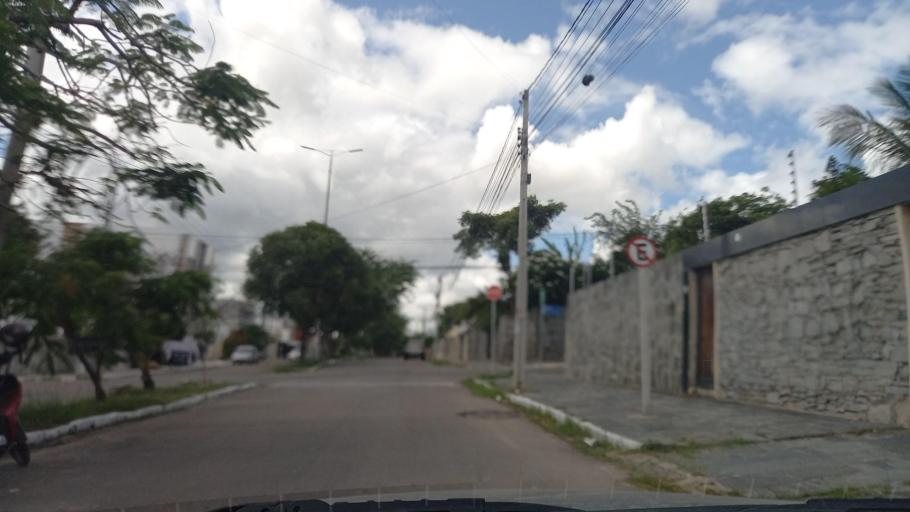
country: BR
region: Pernambuco
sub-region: Caruaru
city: Caruaru
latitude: -8.2971
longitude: -35.9782
